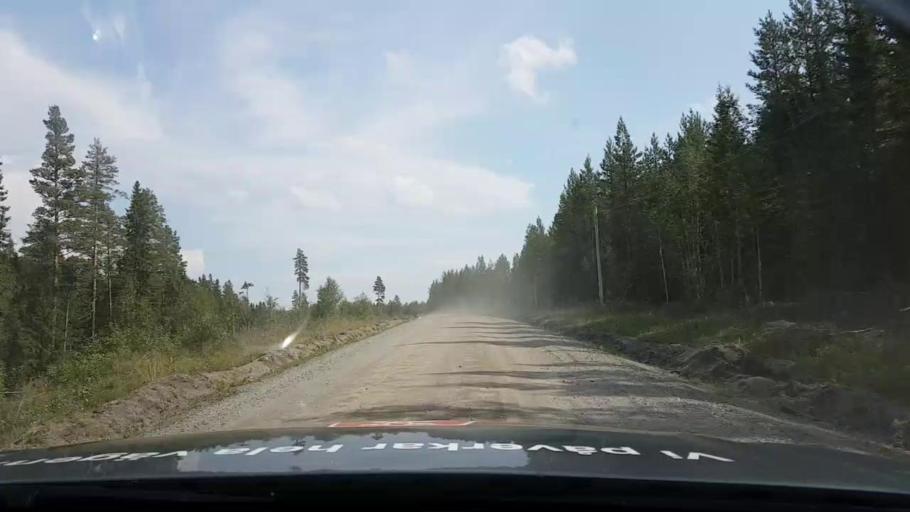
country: SE
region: Jaemtland
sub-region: Braecke Kommun
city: Braecke
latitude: 62.7352
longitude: 15.4643
